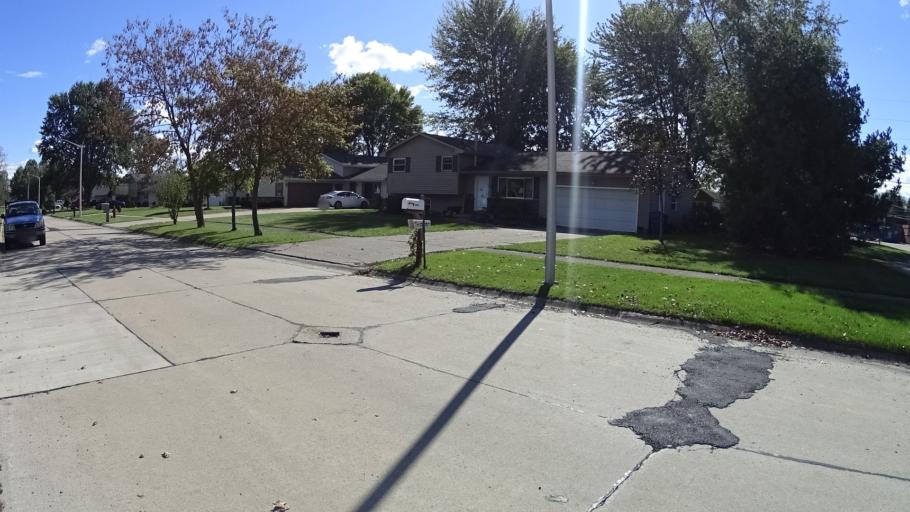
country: US
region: Ohio
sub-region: Lorain County
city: Grafton
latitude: 41.2808
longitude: -82.0626
